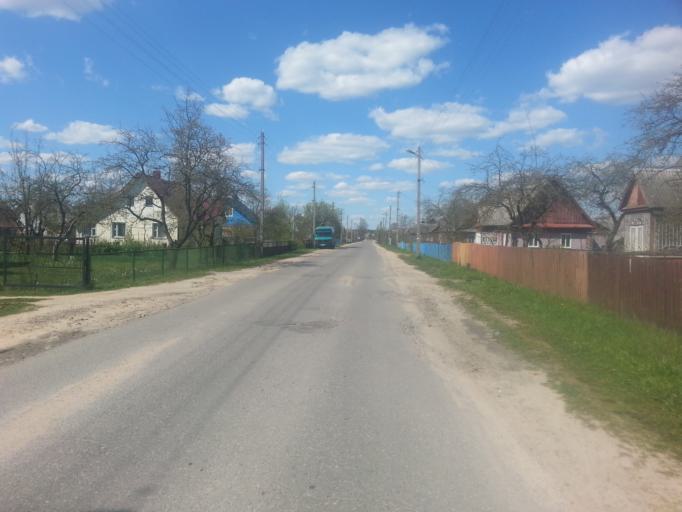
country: BY
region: Minsk
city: Narach
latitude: 54.9289
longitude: 26.6900
